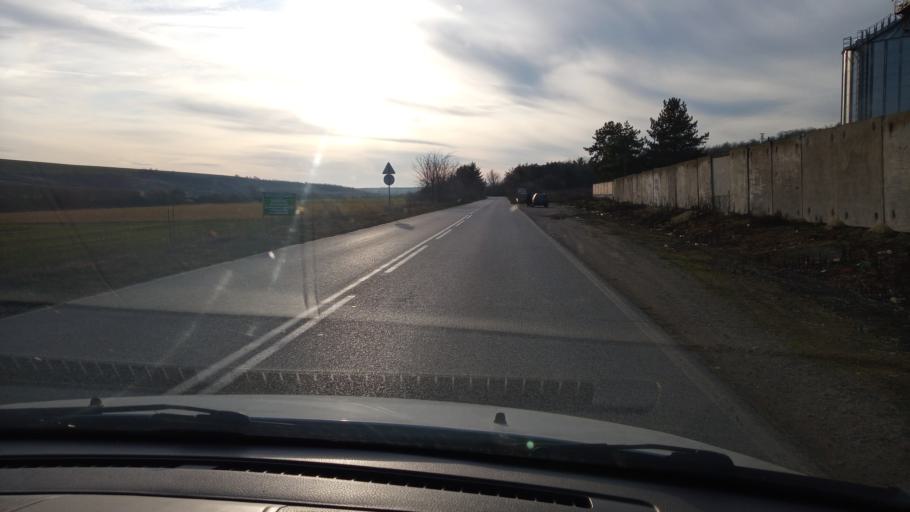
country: BG
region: Pleven
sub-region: Obshtina Pleven
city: Slavyanovo
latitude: 43.5474
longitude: 24.8607
